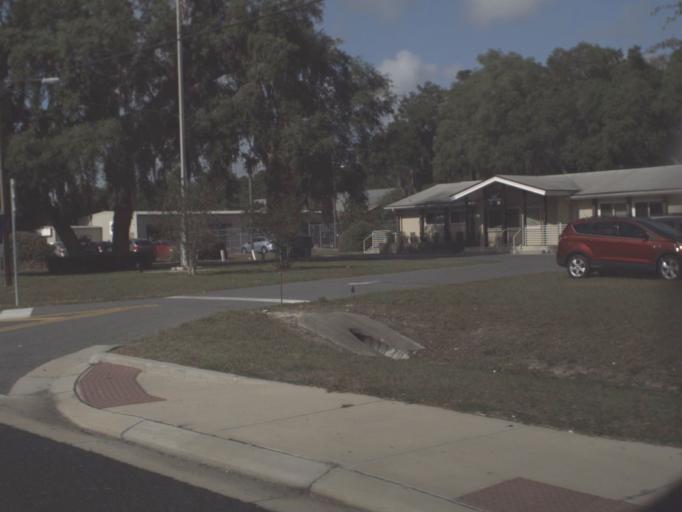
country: US
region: Florida
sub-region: Lake County
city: Fruitland Park
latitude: 28.8743
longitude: -81.9066
